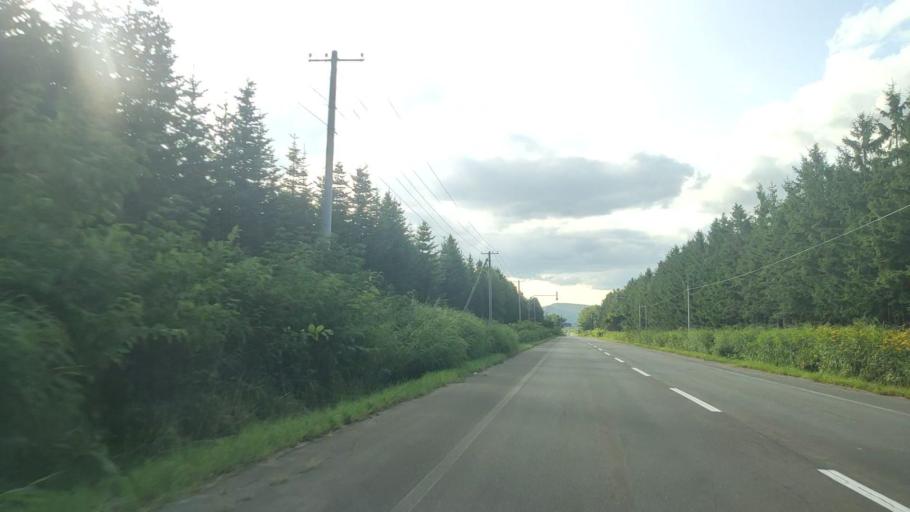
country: JP
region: Hokkaido
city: Makubetsu
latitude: 44.8885
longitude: 142.0049
